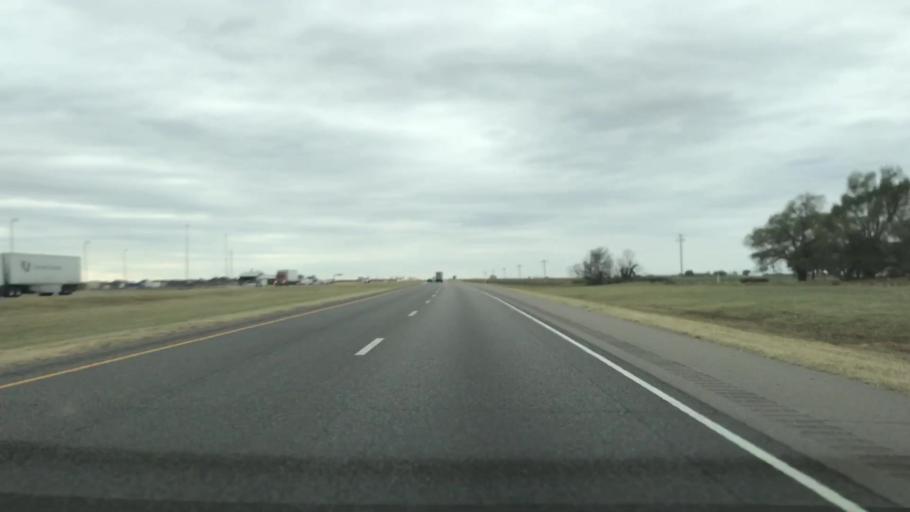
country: US
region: Oklahoma
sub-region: Beckham County
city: Erick
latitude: 35.2318
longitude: -99.9629
